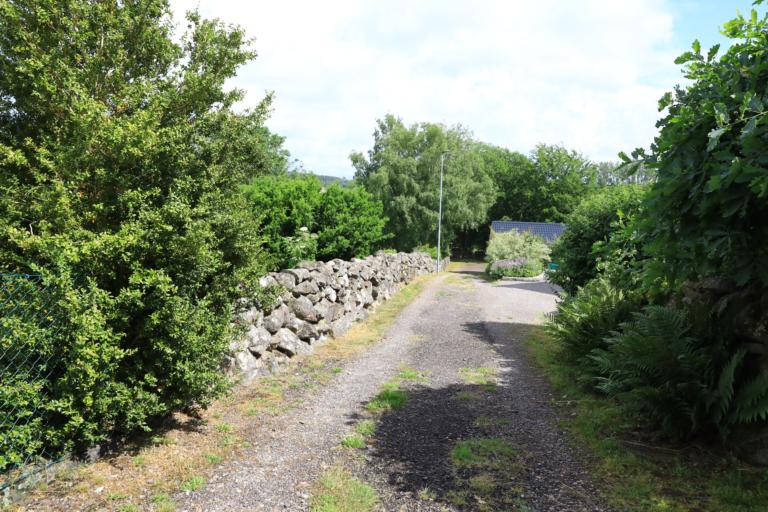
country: SE
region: Halland
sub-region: Varbergs Kommun
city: Varberg
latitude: 57.1752
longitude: 12.2954
